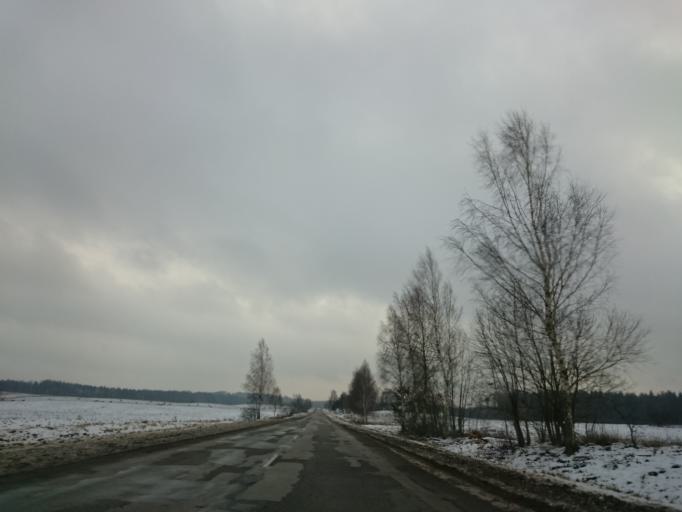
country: LV
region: Pargaujas
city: Stalbe
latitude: 57.3688
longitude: 25.0528
